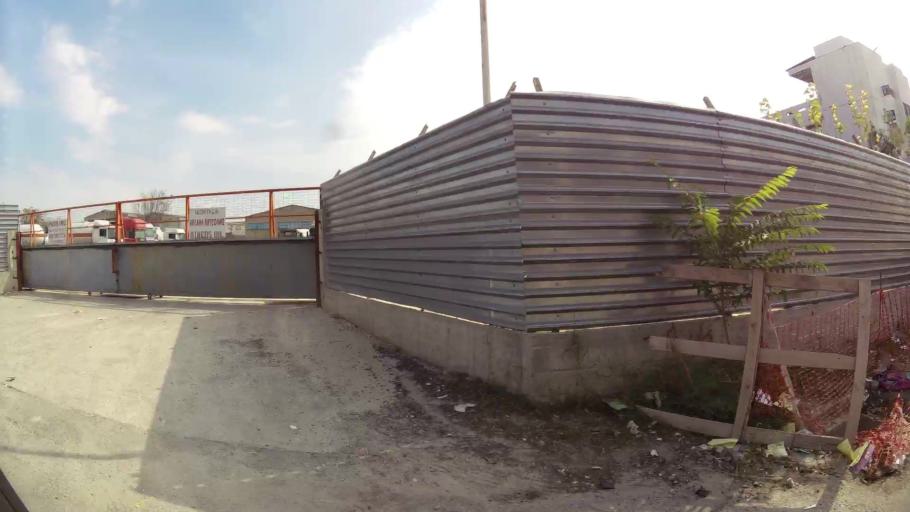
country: GR
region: Attica
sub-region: Nomarchia Athinas
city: Aigaleo
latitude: 37.9910
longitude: 23.6929
